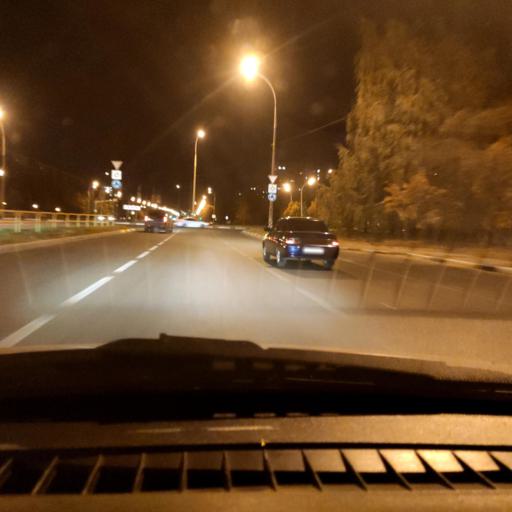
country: RU
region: Samara
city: Tol'yatti
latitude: 53.5263
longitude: 49.3103
